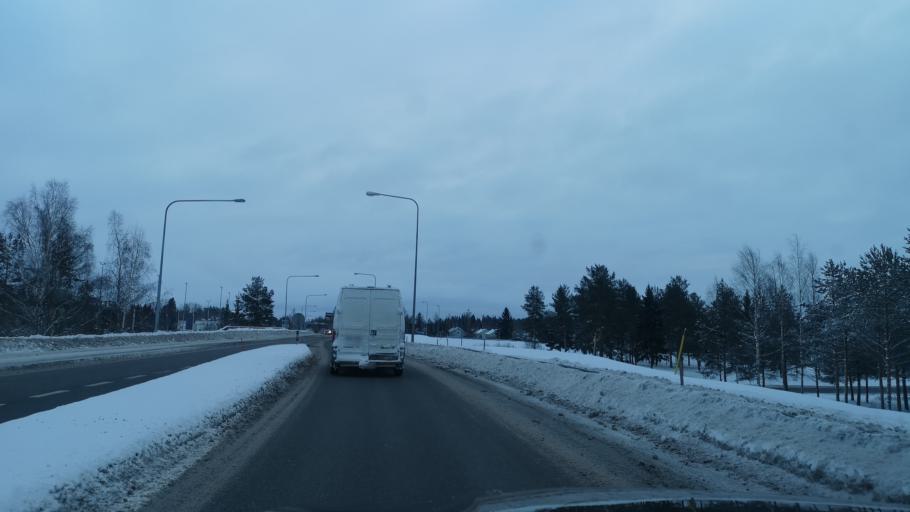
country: FI
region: Varsinais-Suomi
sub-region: Loimaa
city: Loimaa
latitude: 60.8553
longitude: 23.0387
